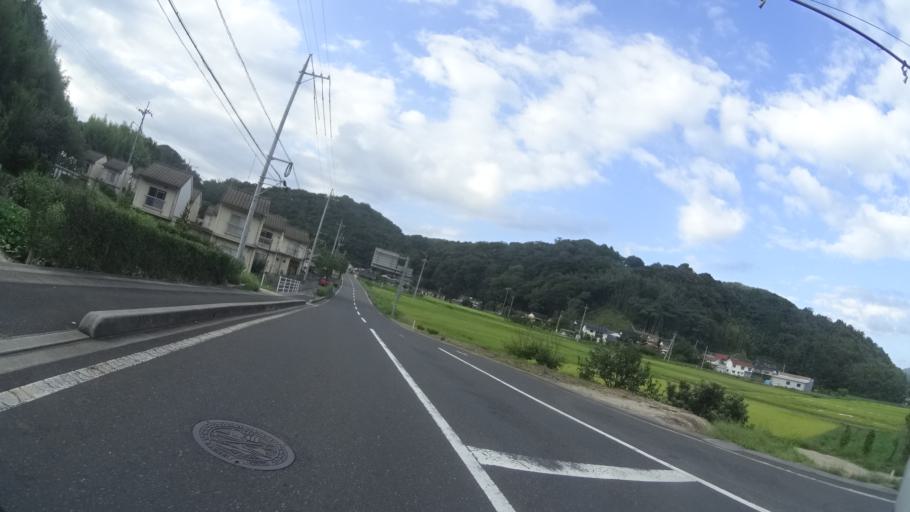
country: JP
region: Tottori
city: Kurayoshi
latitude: 35.4763
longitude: 133.9059
